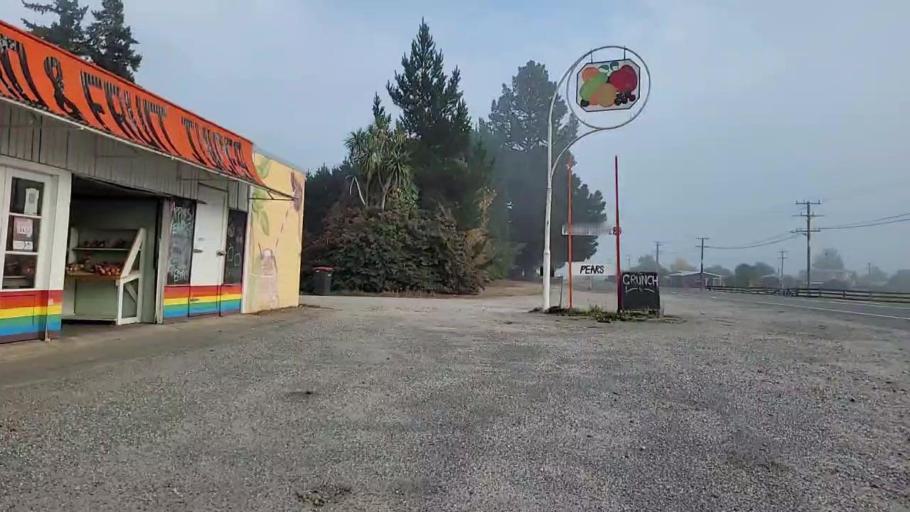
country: NZ
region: Southland
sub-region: Gore District
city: Gore
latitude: -45.6336
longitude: 169.3625
